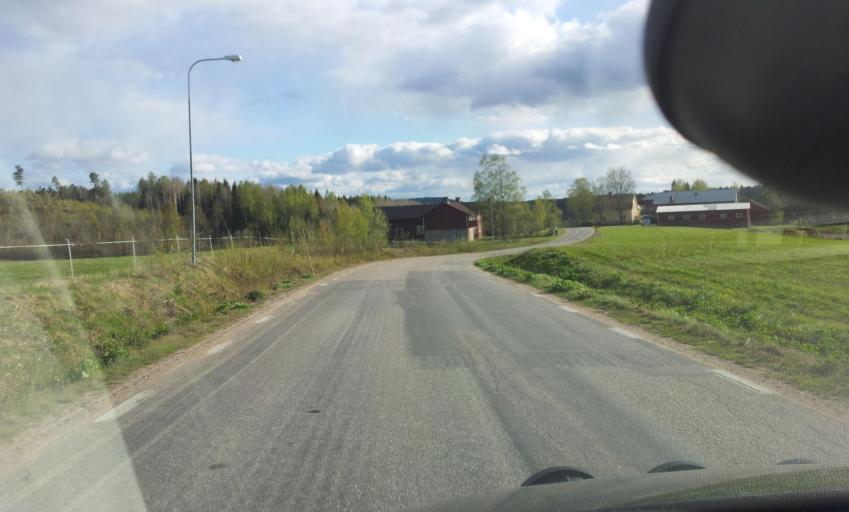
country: SE
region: Gaevleborg
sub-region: Bollnas Kommun
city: Kilafors
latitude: 61.3747
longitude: 16.6201
